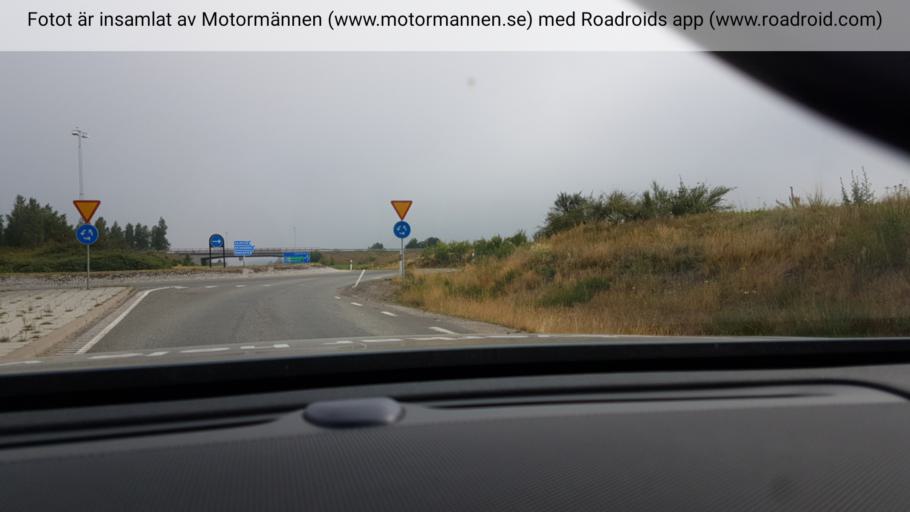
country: SE
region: Skane
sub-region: Hassleholms Kommun
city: Hassleholm
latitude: 56.1788
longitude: 13.7558
